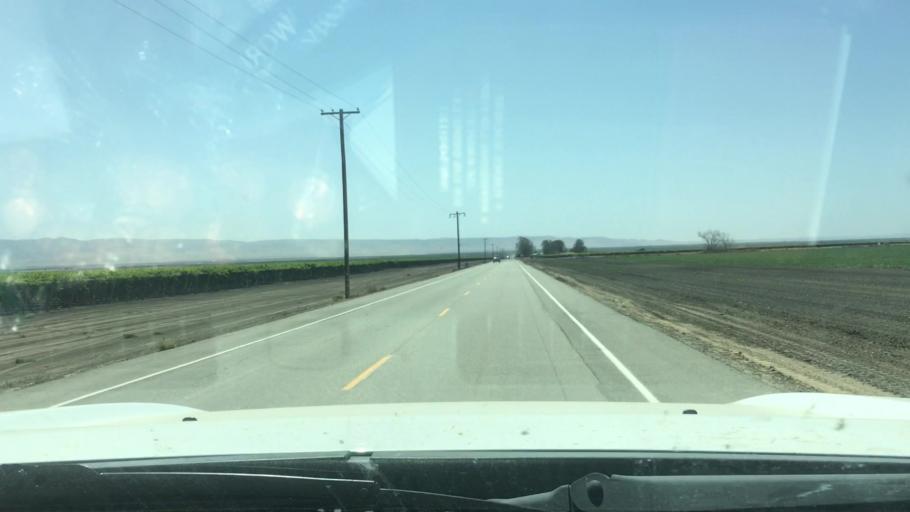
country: US
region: California
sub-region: Kern County
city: Buttonwillow
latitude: 35.4996
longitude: -119.5679
